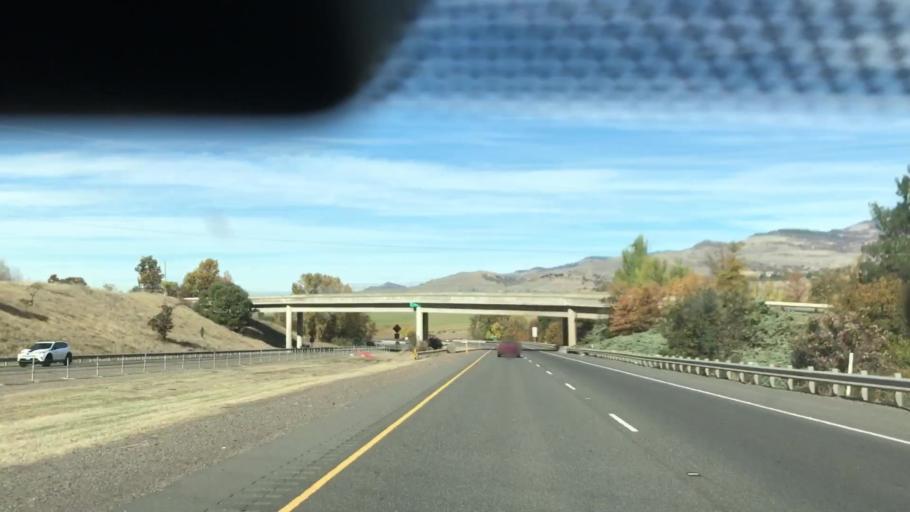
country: US
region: Oregon
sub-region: Jackson County
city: Ashland
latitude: 42.1920
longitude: -122.6705
